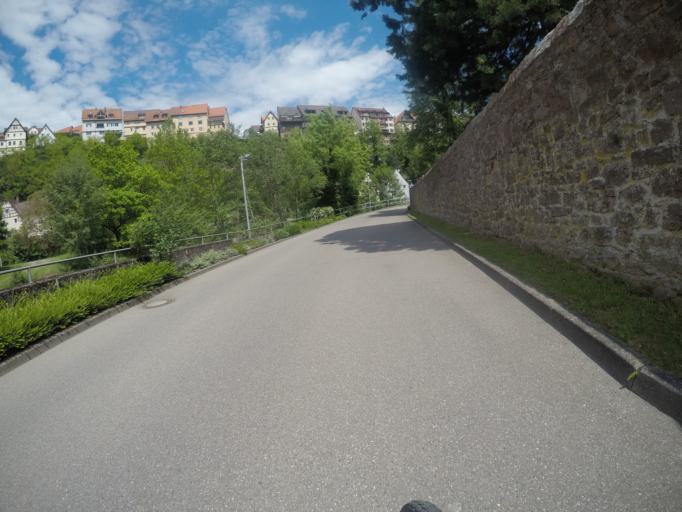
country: DE
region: Baden-Wuerttemberg
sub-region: Karlsruhe Region
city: Wildberg
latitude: 48.6220
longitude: 8.7455
